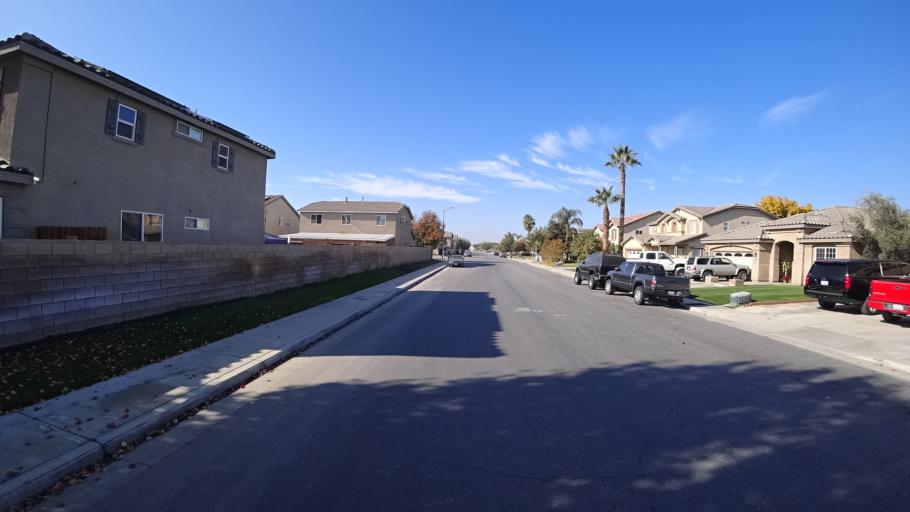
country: US
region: California
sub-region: Kern County
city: Greenfield
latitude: 35.2810
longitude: -119.0593
